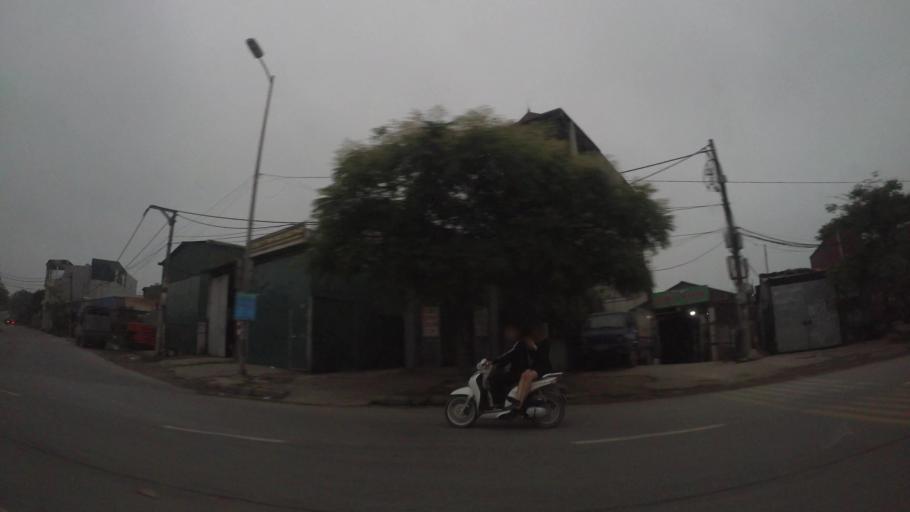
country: VN
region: Ha Noi
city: Van Dien
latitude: 20.9642
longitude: 105.8720
